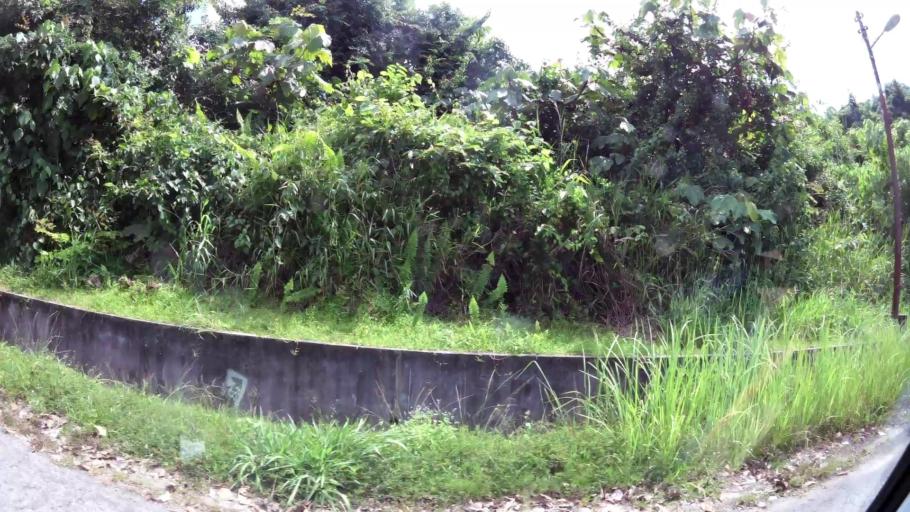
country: BN
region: Brunei and Muara
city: Bandar Seri Begawan
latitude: 4.9796
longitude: 114.9479
